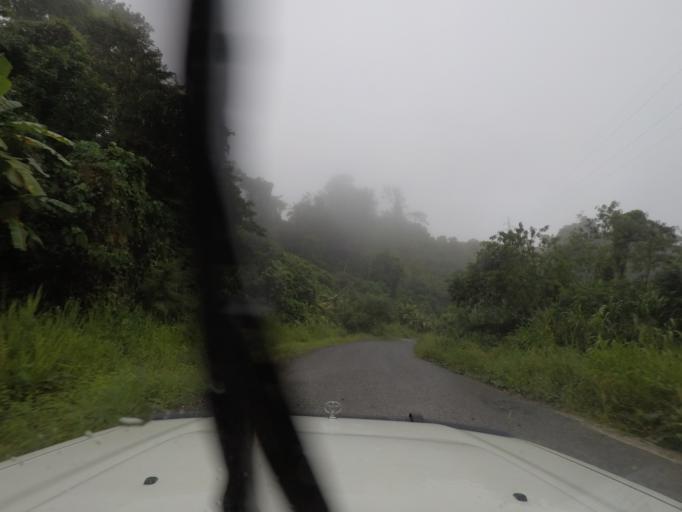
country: PG
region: Madang
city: Madang
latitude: -5.4029
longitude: 145.5862
